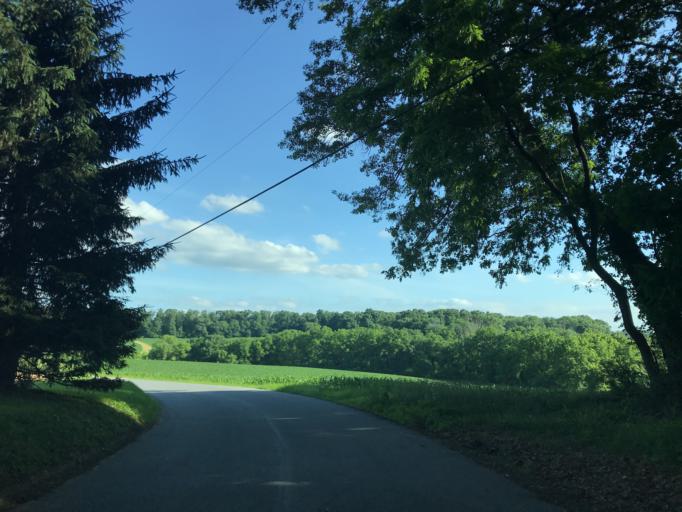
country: US
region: Maryland
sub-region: Baltimore County
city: Reisterstown
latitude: 39.5219
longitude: -76.8438
